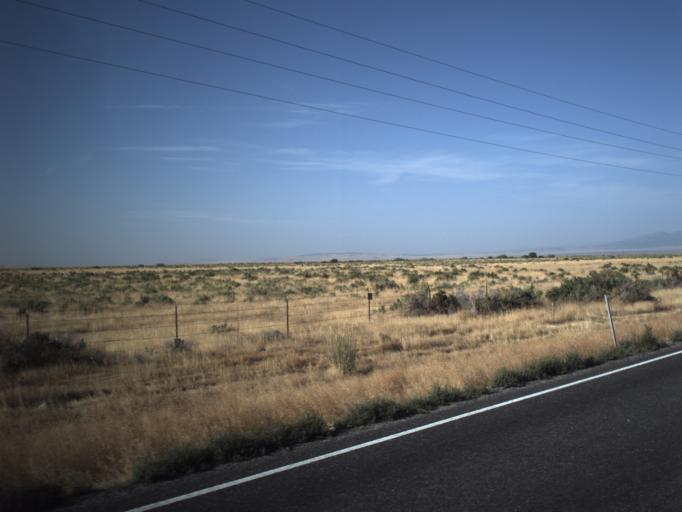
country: US
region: Idaho
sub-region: Oneida County
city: Malad City
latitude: 41.9668
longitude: -112.7894
